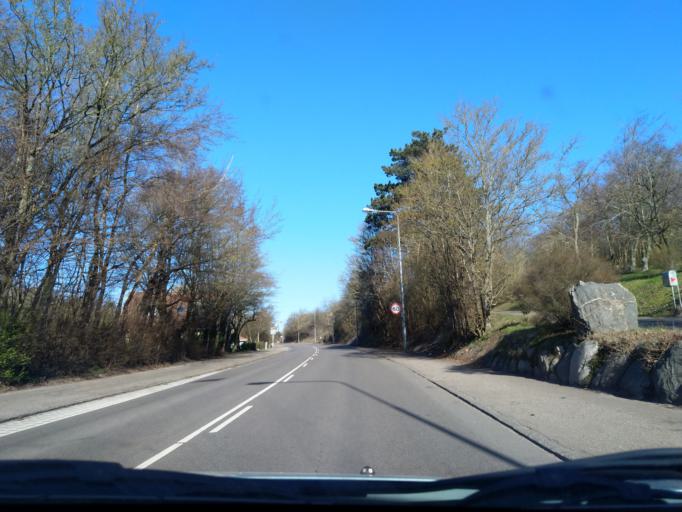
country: DK
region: Zealand
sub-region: Kalundborg Kommune
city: Kalundborg
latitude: 55.6989
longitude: 11.0384
